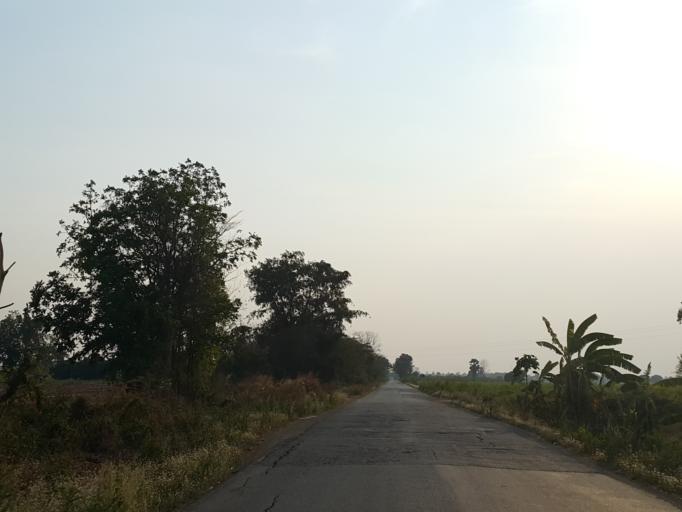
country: TH
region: Sukhothai
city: Si Samrong
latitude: 17.2211
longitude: 99.9279
